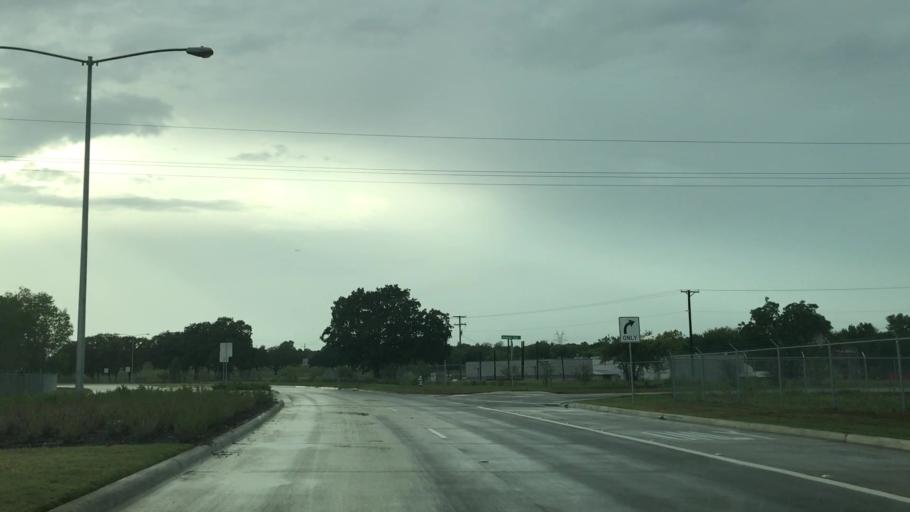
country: US
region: Texas
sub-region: Denton County
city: Lewisville
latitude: 33.0562
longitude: -96.9836
